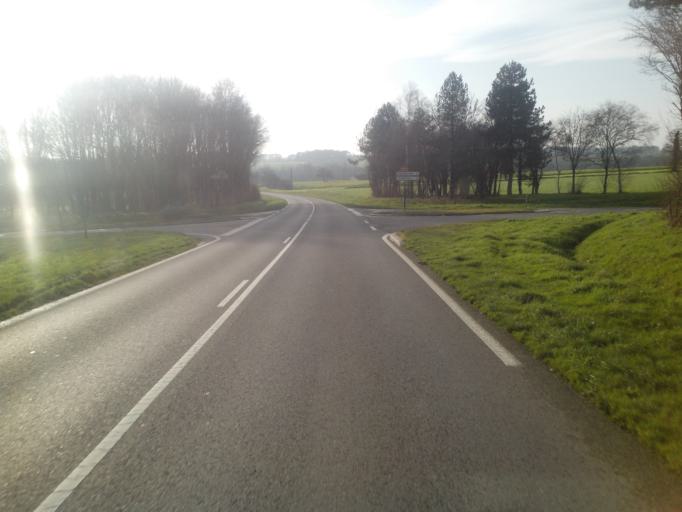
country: FR
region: Brittany
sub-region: Departement d'Ille-et-Vilaine
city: Gael
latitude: 48.1370
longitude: -2.2268
